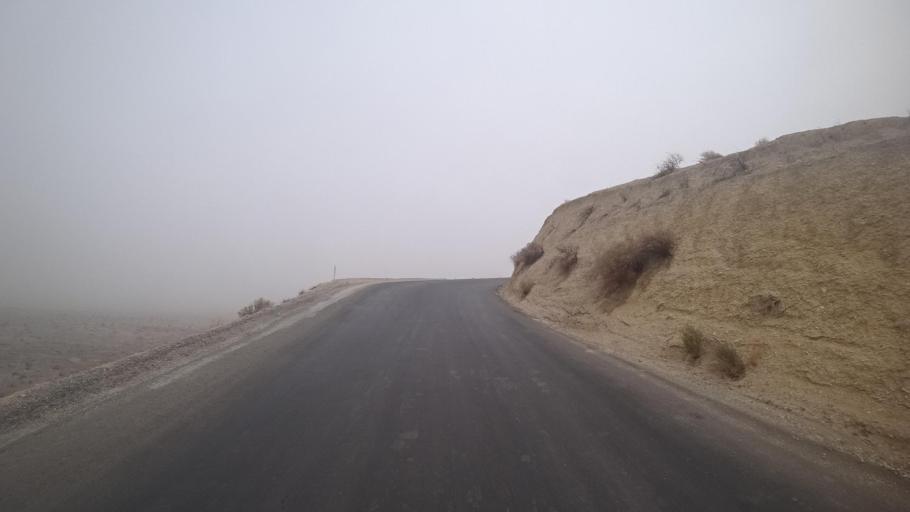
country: US
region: California
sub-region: Kern County
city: Maricopa
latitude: 35.0406
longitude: -119.4291
